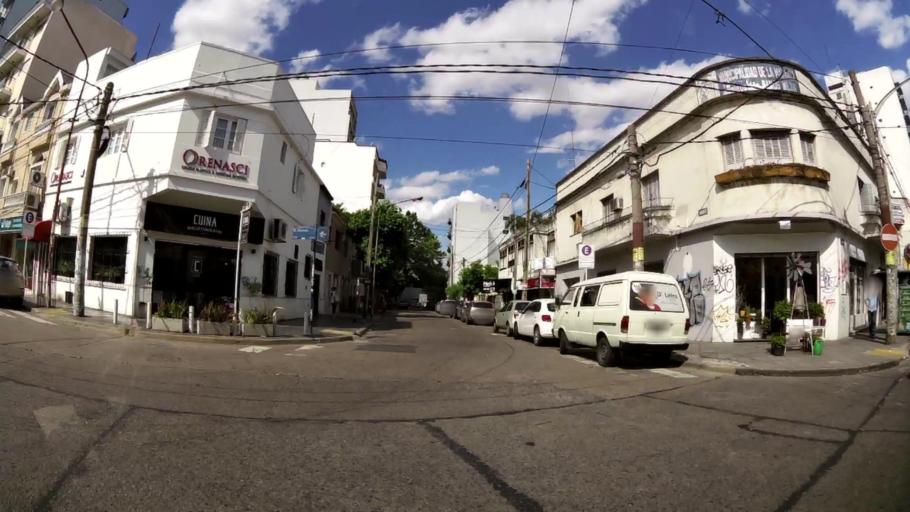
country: AR
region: Buenos Aires
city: San Justo
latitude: -34.6432
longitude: -58.5624
